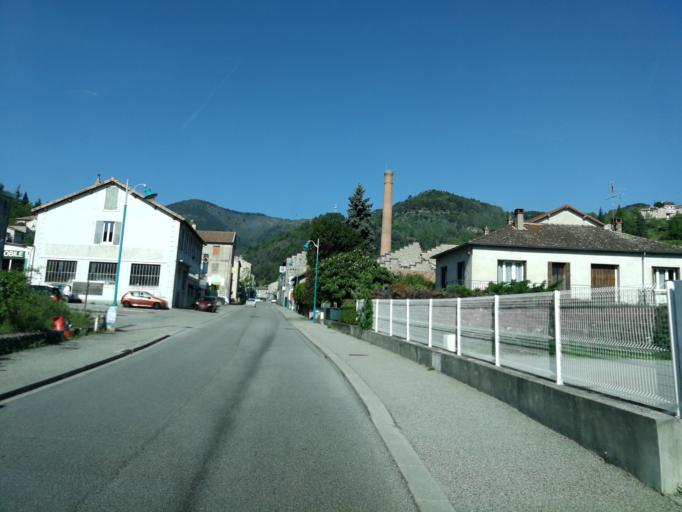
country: FR
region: Rhone-Alpes
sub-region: Departement de l'Ardeche
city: Saint-Sauveur-de-Montagut
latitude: 44.8214
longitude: 4.5862
